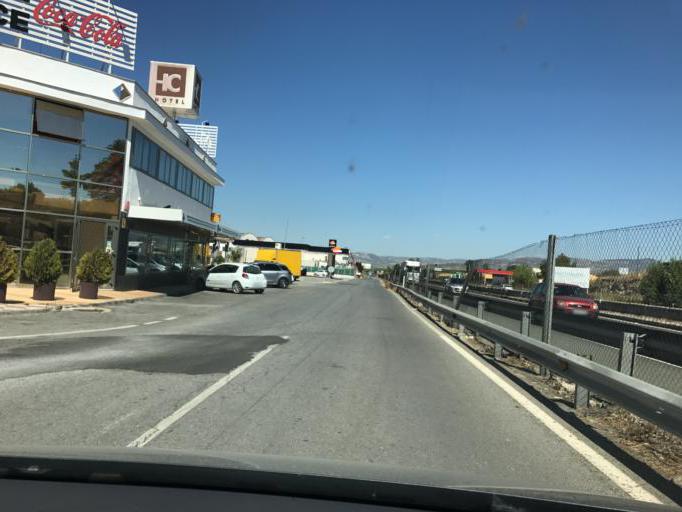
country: ES
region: Andalusia
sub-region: Provincia de Granada
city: Moraleda de Zafayona
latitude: 37.1845
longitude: -3.9576
